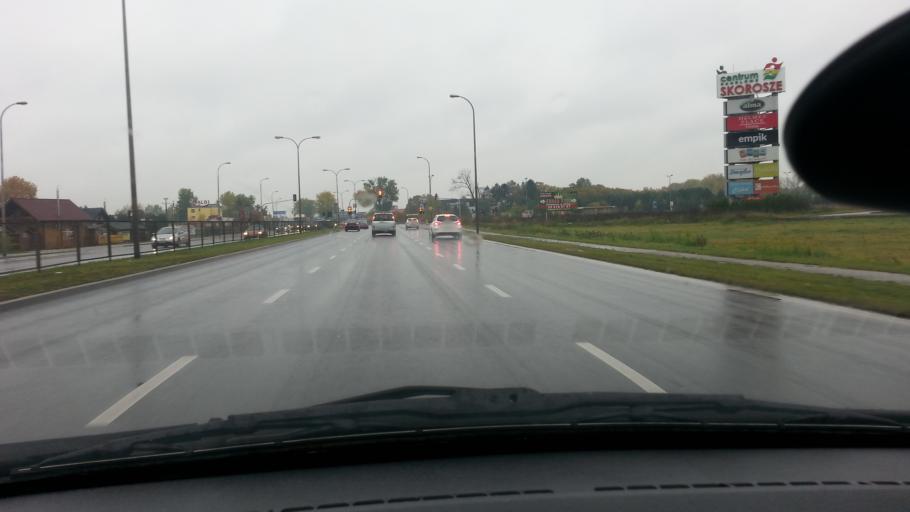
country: PL
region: Masovian Voivodeship
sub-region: Warszawa
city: Ursus
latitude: 52.1847
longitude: 20.8998
